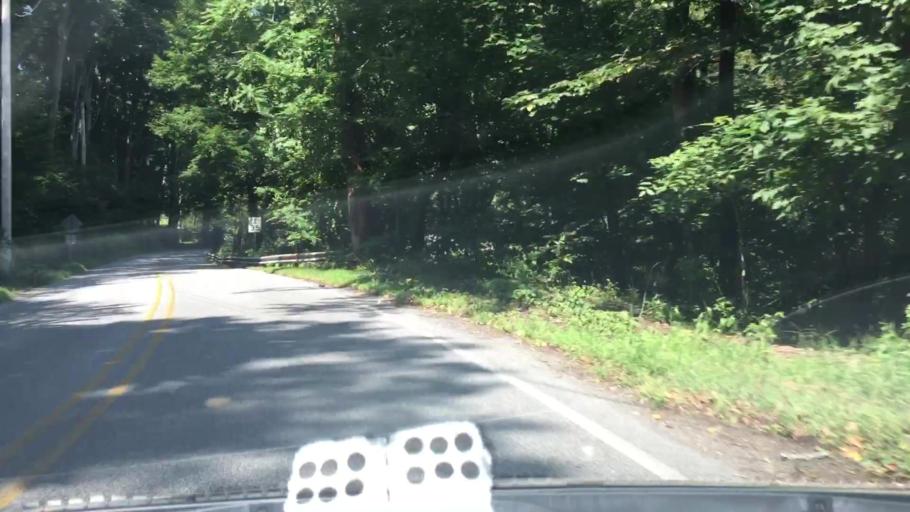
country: US
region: Pennsylvania
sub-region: Delaware County
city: Media
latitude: 39.9025
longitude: -75.3926
